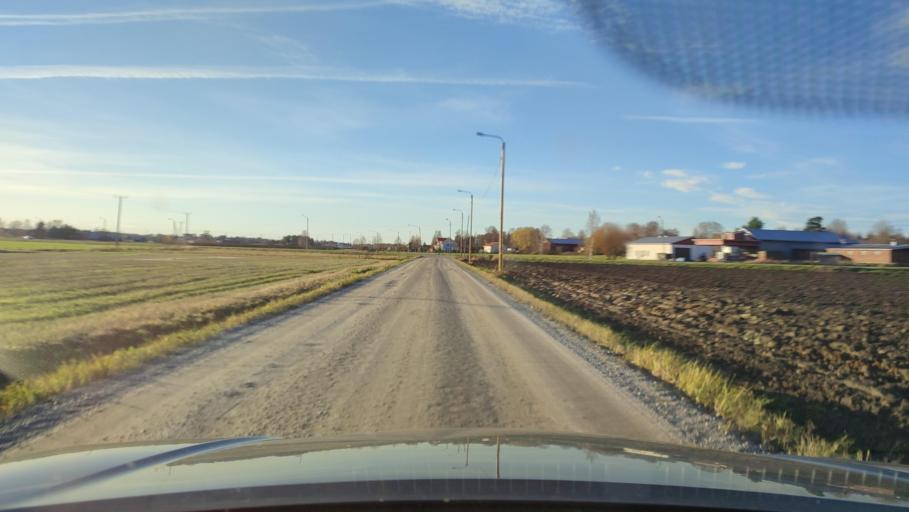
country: FI
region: Ostrobothnia
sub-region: Vaasa
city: Ristinummi
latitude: 63.0109
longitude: 21.7022
